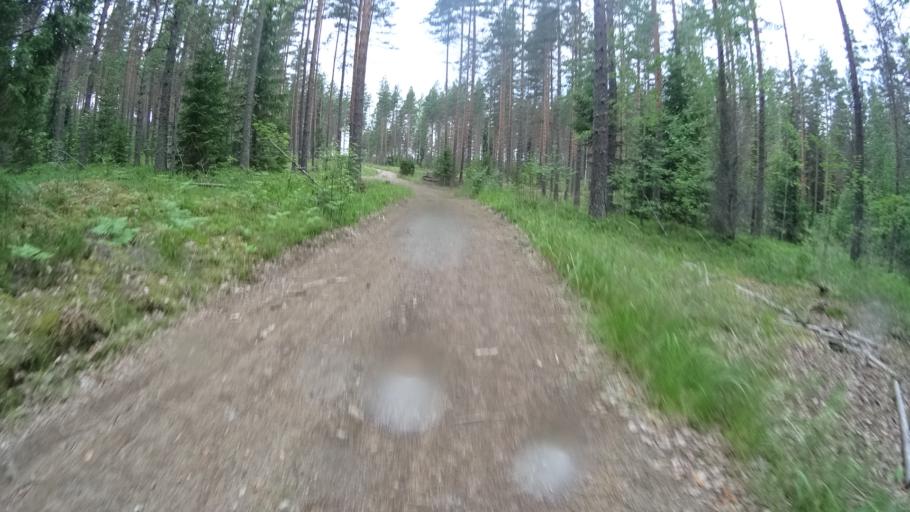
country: FI
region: Uusimaa
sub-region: Helsinki
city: Karkkila
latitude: 60.5956
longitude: 24.1886
